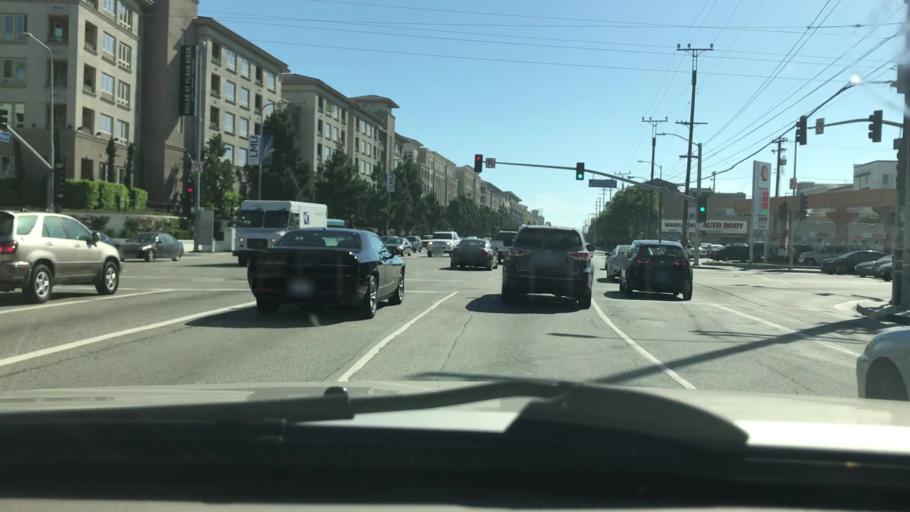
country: US
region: California
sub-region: Los Angeles County
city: Ladera Heights
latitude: 33.9815
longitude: -118.4088
